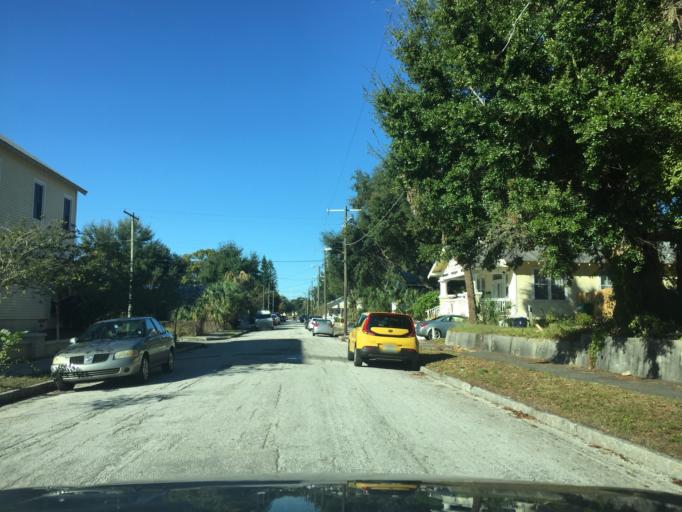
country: US
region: Florida
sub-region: Hillsborough County
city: Tampa
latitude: 27.9633
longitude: -82.4479
